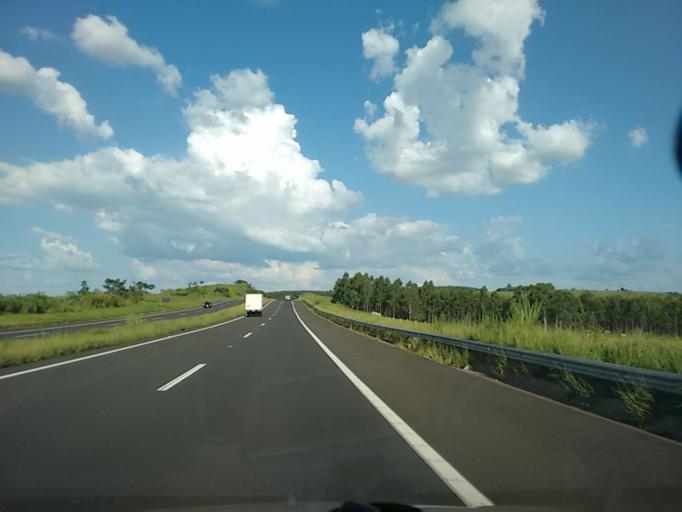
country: BR
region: Sao Paulo
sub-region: Duartina
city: Duartina
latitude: -22.3189
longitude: -49.4891
